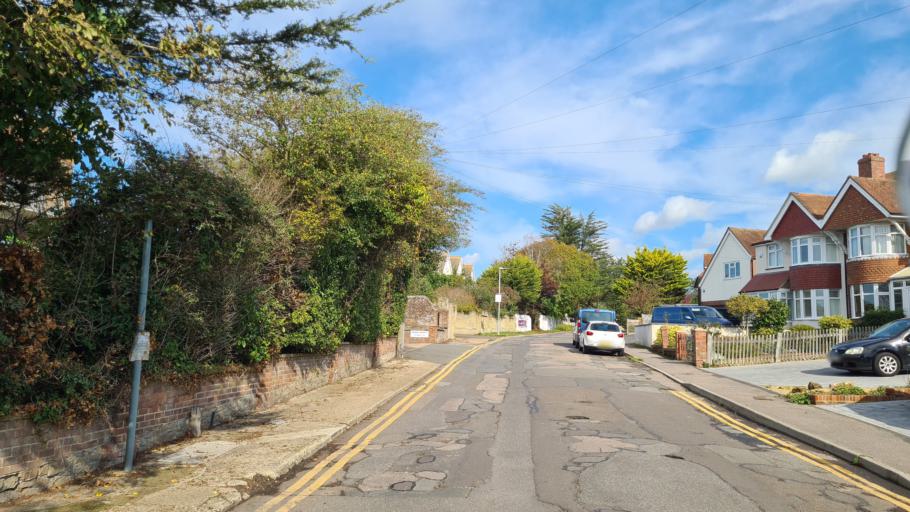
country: GB
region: England
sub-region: East Sussex
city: Saint Leonards-on-Sea
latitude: 50.8761
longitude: 0.5587
